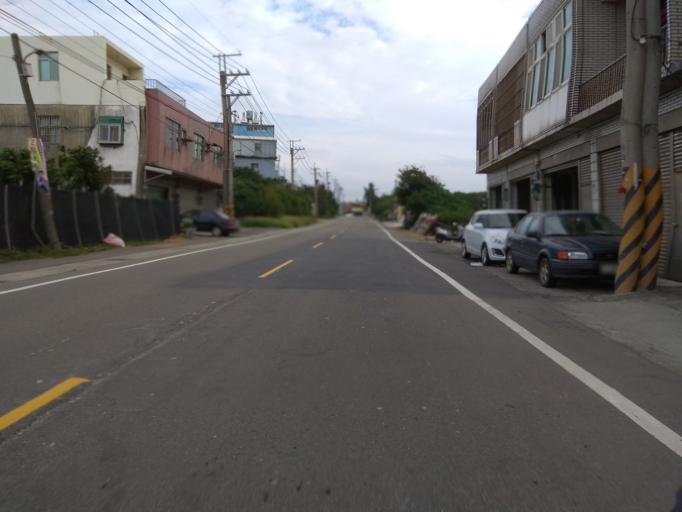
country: TW
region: Taiwan
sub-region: Hsinchu
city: Zhubei
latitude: 24.9853
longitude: 121.0414
